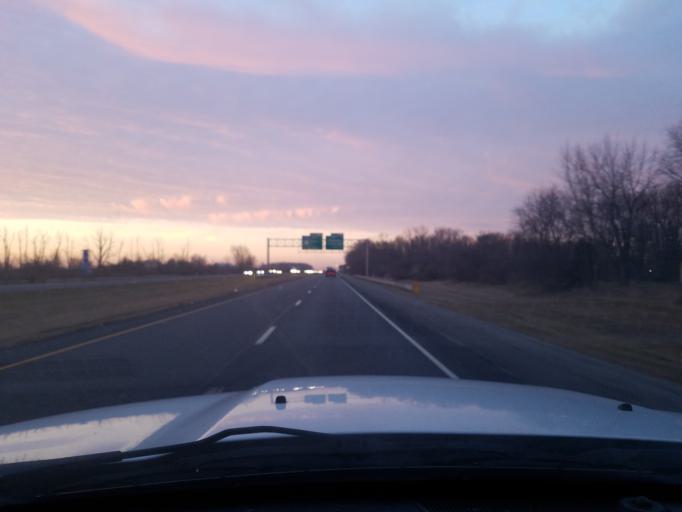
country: US
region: Indiana
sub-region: Huntington County
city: Roanoke
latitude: 40.9793
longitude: -85.2775
